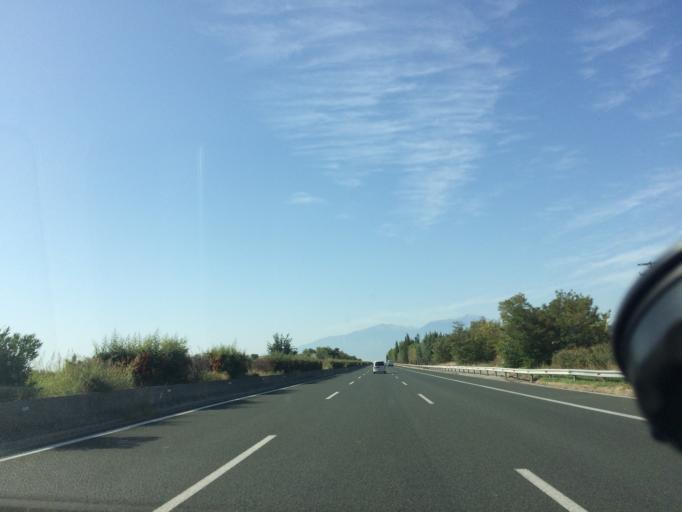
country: GR
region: Central Macedonia
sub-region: Nomos Pierias
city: Kitros
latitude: 40.3556
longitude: 22.5988
